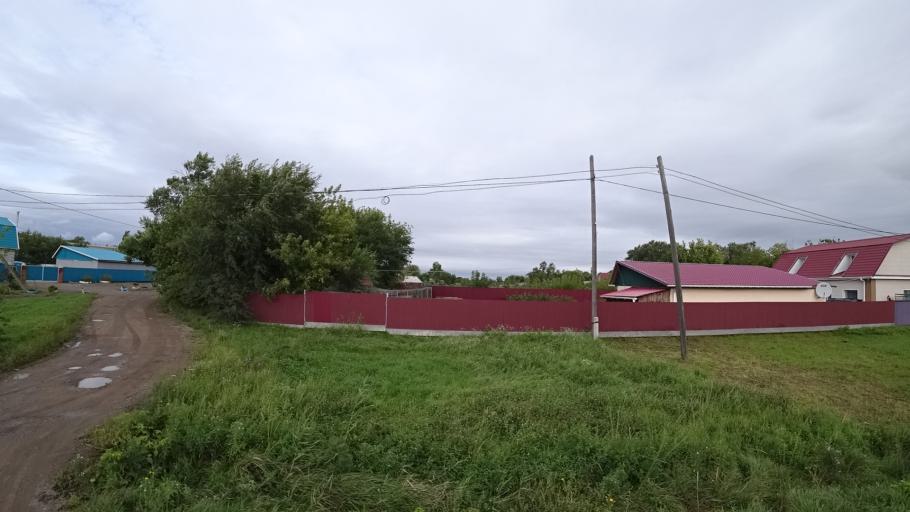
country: RU
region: Primorskiy
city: Chernigovka
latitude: 44.3339
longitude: 132.5765
